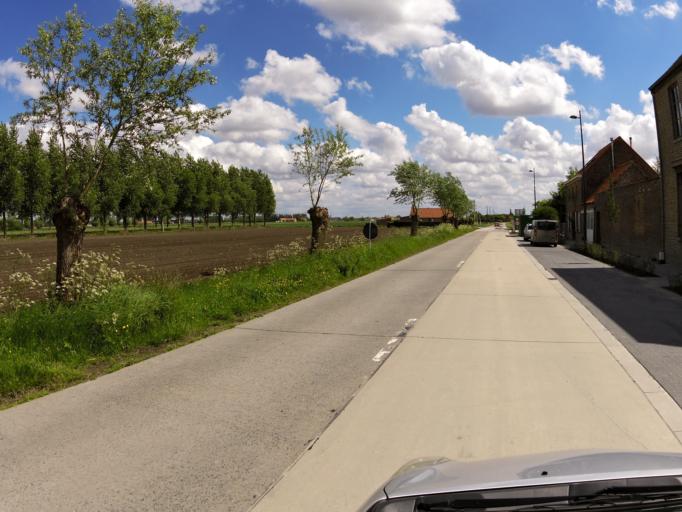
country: BE
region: Flanders
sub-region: Provincie West-Vlaanderen
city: Gistel
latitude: 51.1192
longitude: 2.9239
